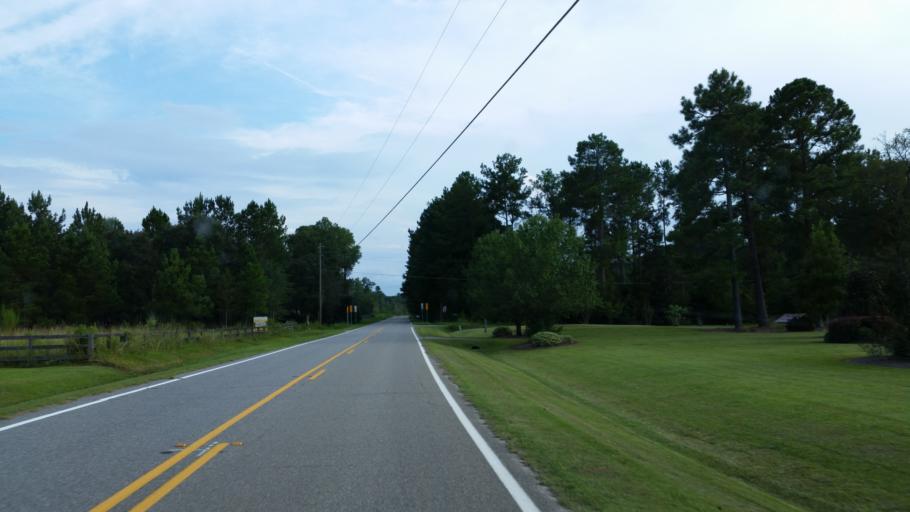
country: US
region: Georgia
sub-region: Lowndes County
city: Hahira
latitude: 31.0161
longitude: -83.3876
